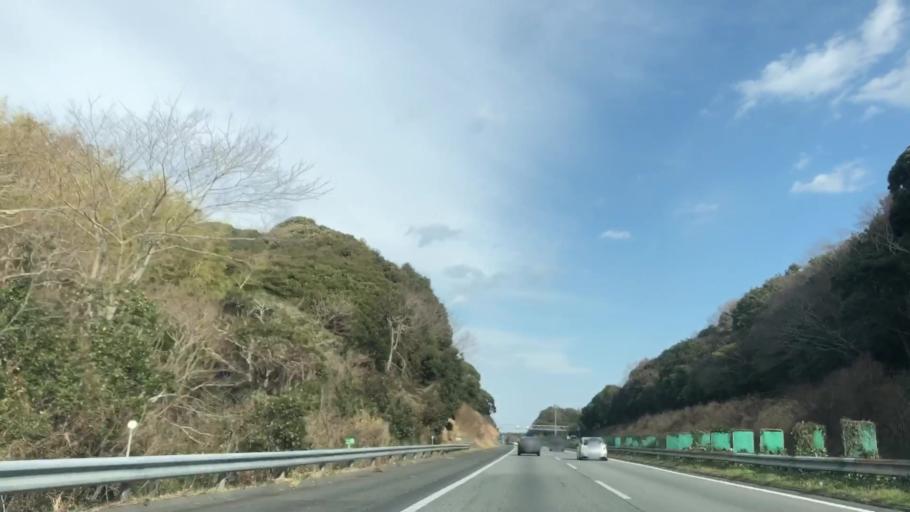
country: JP
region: Shizuoka
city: Fukuroi
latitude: 34.7644
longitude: 137.9420
